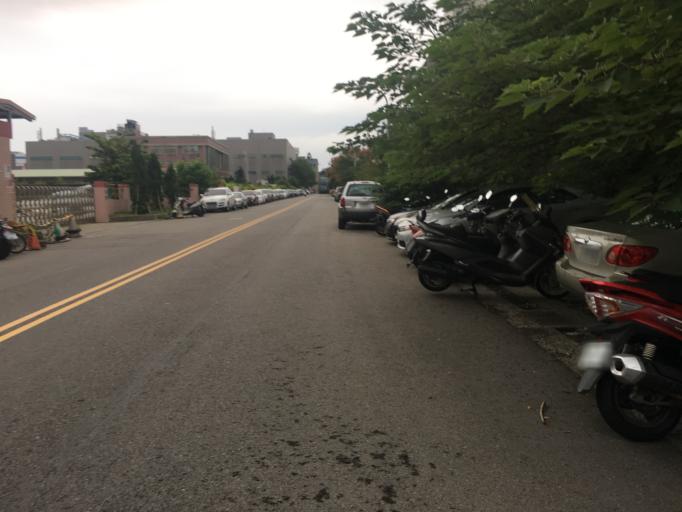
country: TW
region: Taiwan
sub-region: Hsinchu
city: Hsinchu
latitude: 24.7255
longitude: 120.9102
